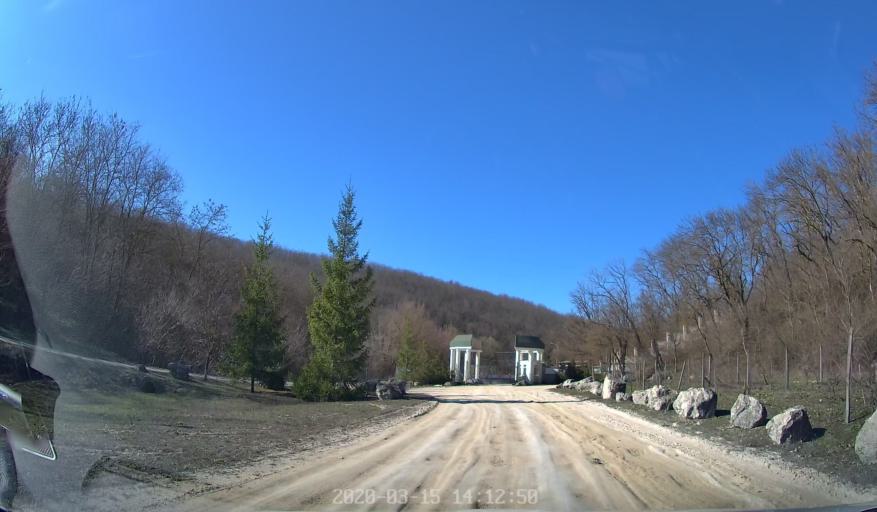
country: MD
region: Orhei
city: Orhei
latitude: 47.3148
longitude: 28.9376
